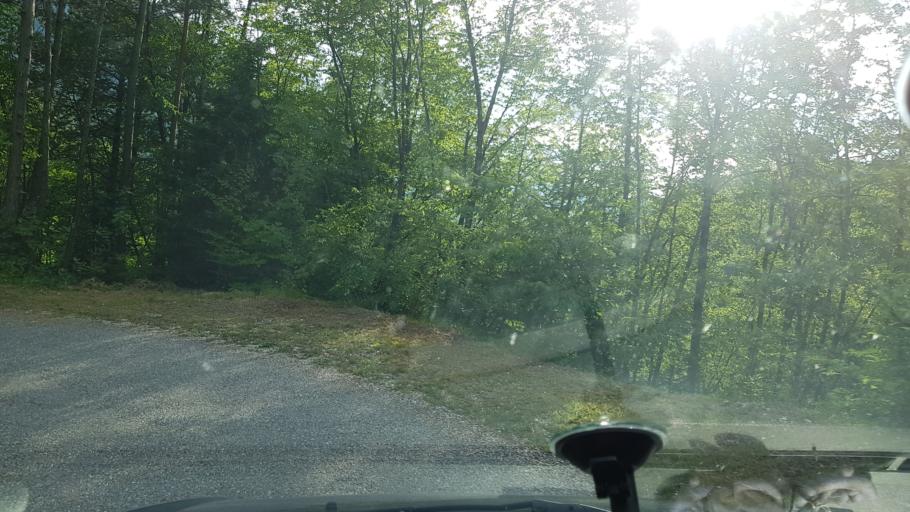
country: IT
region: Friuli Venezia Giulia
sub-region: Provincia di Udine
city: Prato
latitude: 46.3584
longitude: 13.3645
